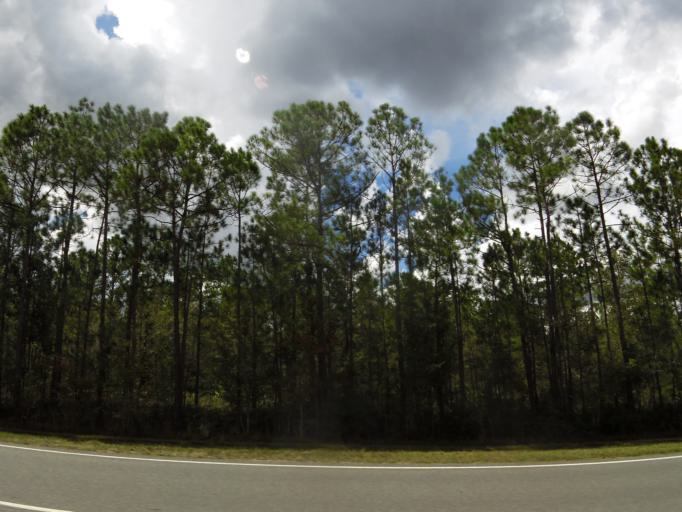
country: US
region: Georgia
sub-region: Brantley County
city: Nahunta
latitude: 31.1808
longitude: -81.9878
